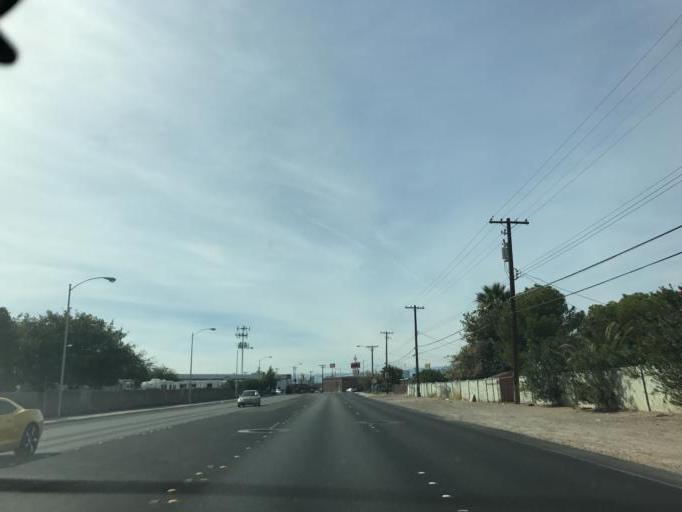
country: US
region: Nevada
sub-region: Clark County
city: Winchester
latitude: 36.1296
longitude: -115.0791
